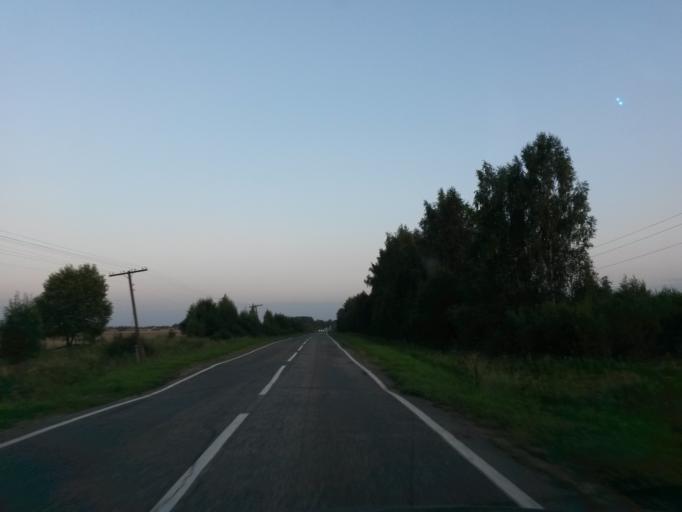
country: RU
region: Jaroslavl
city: Tutayev
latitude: 57.9096
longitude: 39.5189
